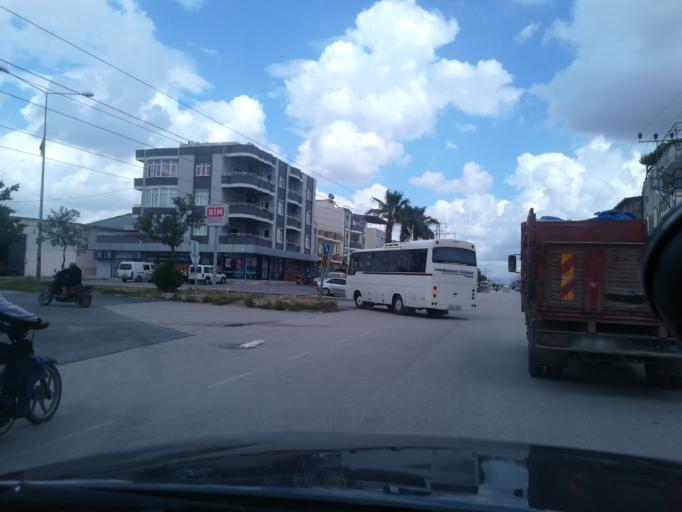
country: TR
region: Adana
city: Yuregir
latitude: 36.9772
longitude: 35.3843
